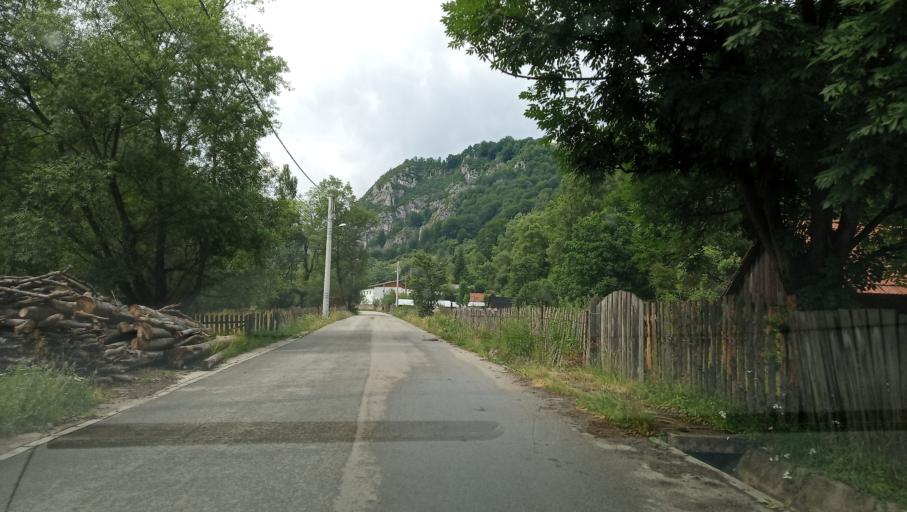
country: RO
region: Hunedoara
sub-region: Oras Petrila
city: Petrila
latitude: 45.4634
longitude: 23.4203
